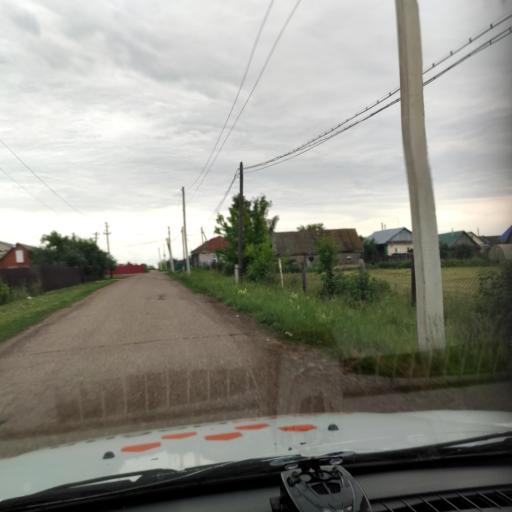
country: RU
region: Bashkortostan
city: Kabakovo
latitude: 54.4565
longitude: 55.9528
